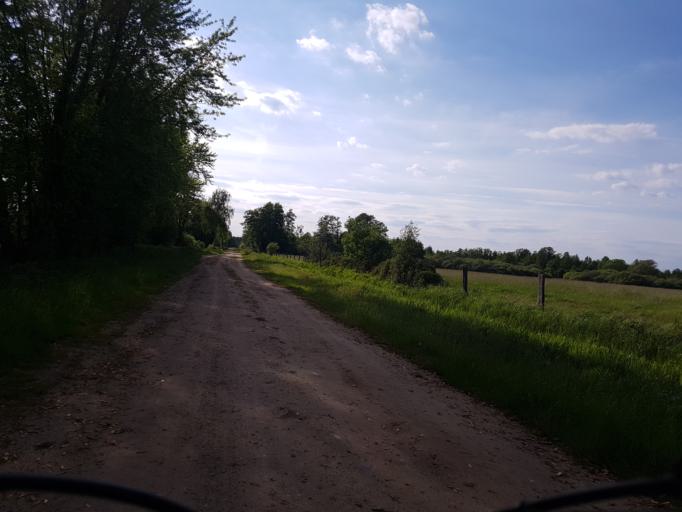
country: DE
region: Brandenburg
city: Groden
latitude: 51.4165
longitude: 13.5598
